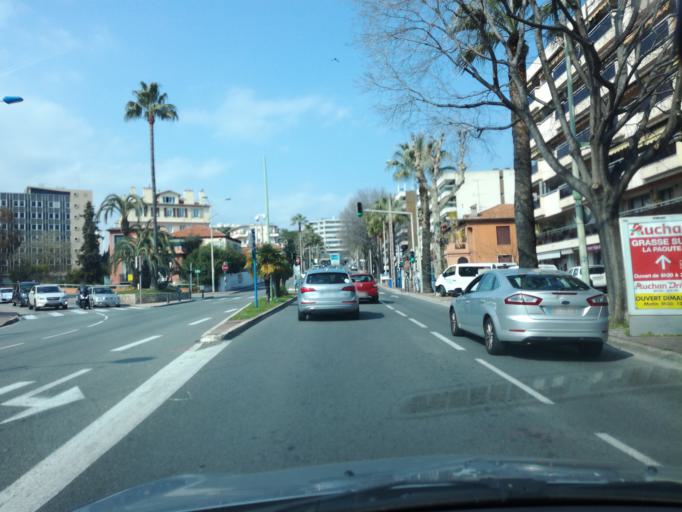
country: FR
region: Provence-Alpes-Cote d'Azur
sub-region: Departement des Alpes-Maritimes
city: Le Cannet
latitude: 43.5692
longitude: 7.0164
